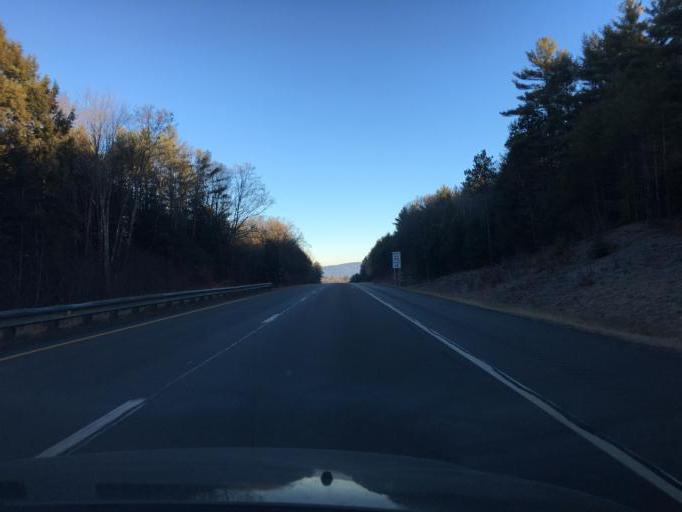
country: US
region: New Hampshire
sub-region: Belknap County
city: Sanbornton
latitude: 43.5140
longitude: -71.6154
